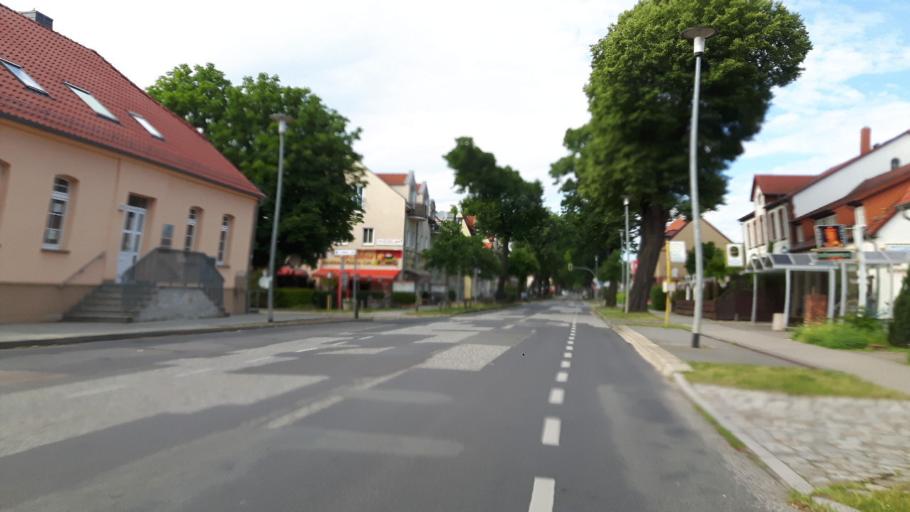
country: DE
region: Brandenburg
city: Michendorf
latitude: 52.3107
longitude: 13.0295
